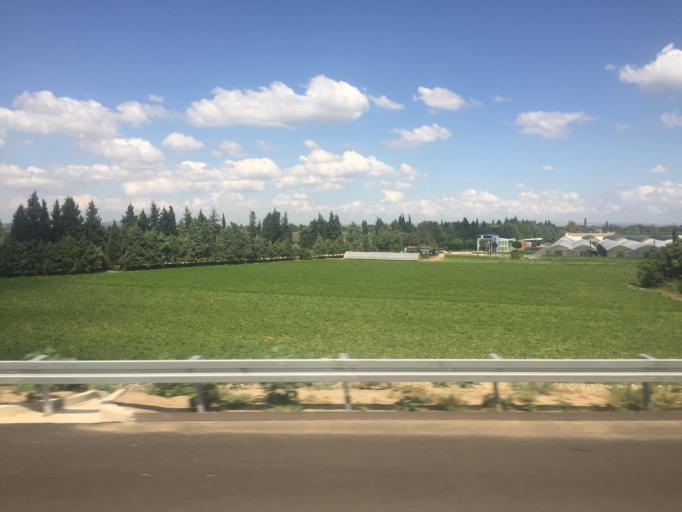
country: TR
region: Balikesir
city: Gobel
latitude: 40.0715
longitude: 28.2514
